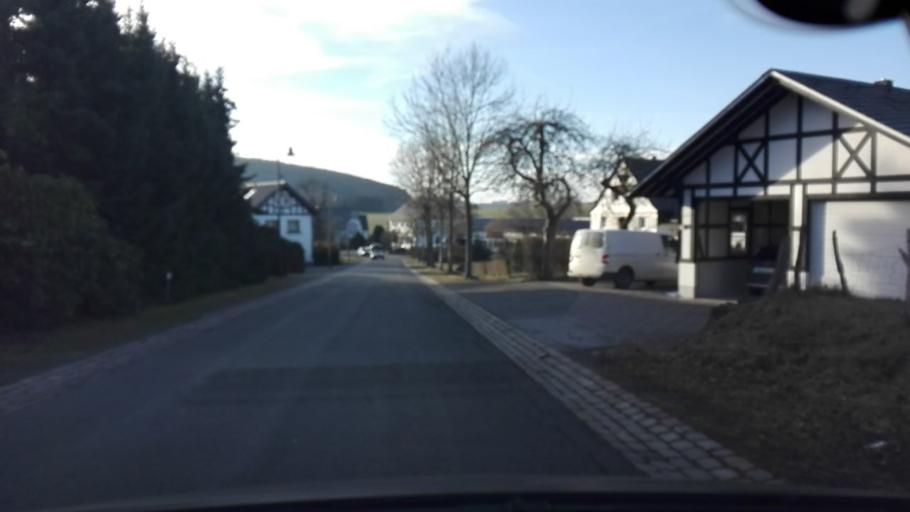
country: DE
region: North Rhine-Westphalia
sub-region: Regierungsbezirk Arnsberg
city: Schmallenberg
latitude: 51.1558
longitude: 8.2520
